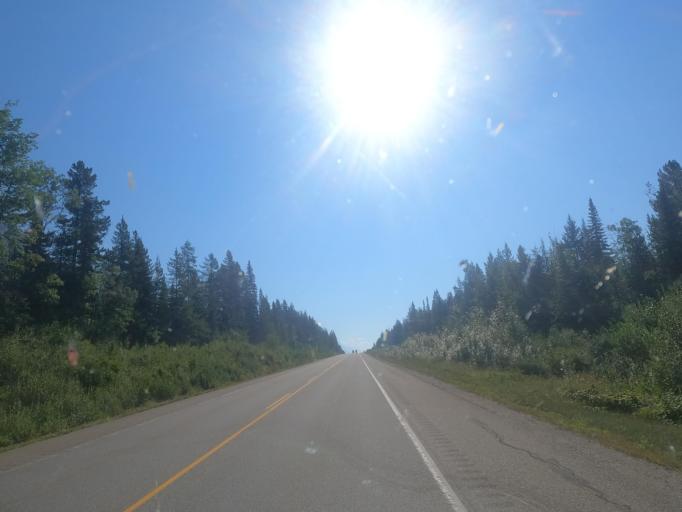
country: CA
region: Alberta
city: Jasper Park Lodge
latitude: 52.9781
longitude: -118.9698
